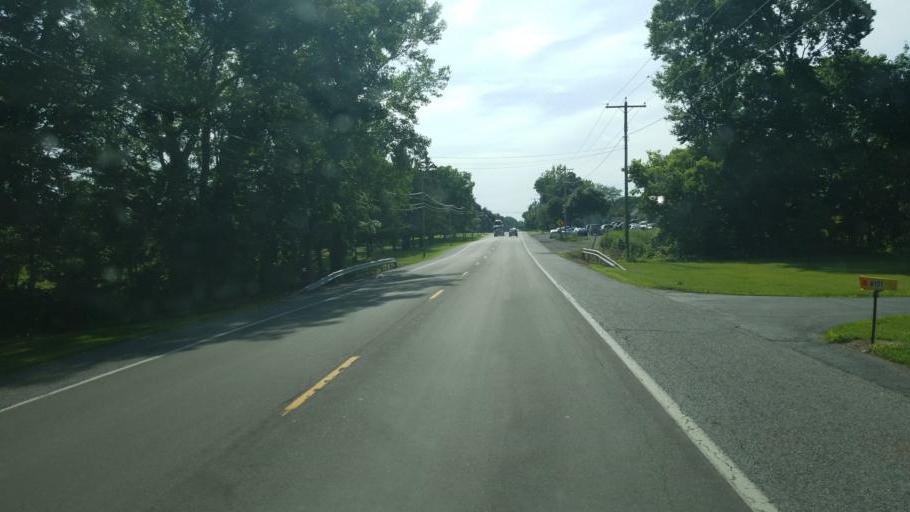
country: US
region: New York
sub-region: Genesee County
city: Le Roy
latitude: 42.9795
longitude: -77.9427
